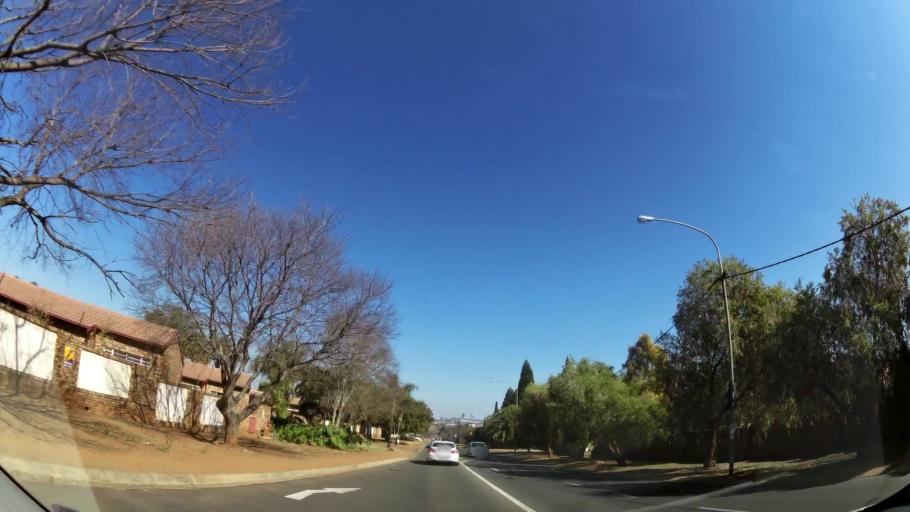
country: ZA
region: Gauteng
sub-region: City of Tshwane Metropolitan Municipality
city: Centurion
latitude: -25.8539
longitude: 28.2020
